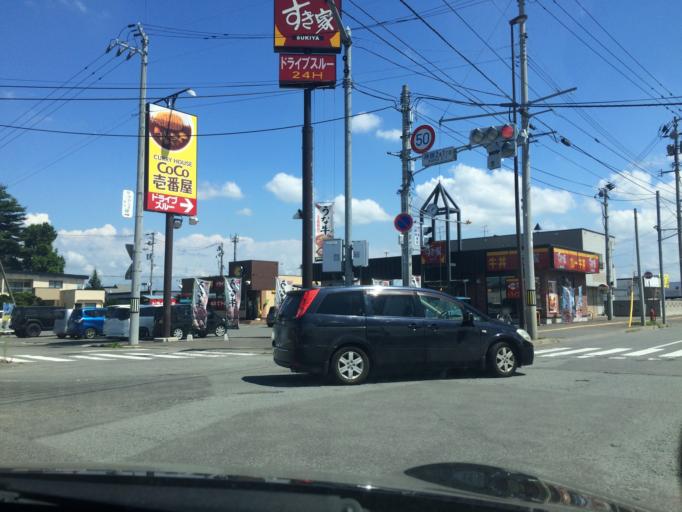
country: JP
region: Hokkaido
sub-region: Asahikawa-shi
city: Asahikawa
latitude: 43.7698
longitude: 142.3292
